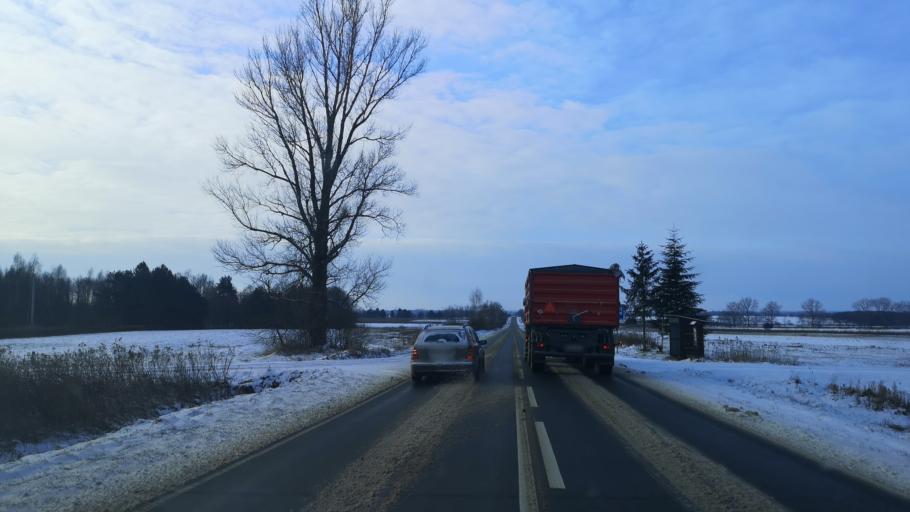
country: PL
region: Subcarpathian Voivodeship
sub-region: Powiat przeworski
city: Sieniawa
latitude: 50.2036
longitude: 22.6354
